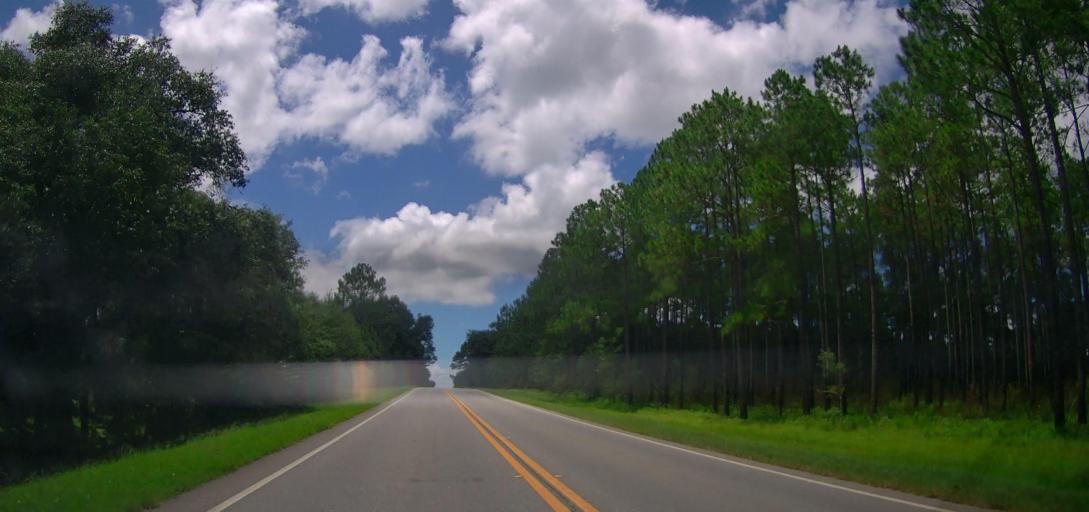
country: US
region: Georgia
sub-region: Turner County
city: Ashburn
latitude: 31.7223
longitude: -83.5635
